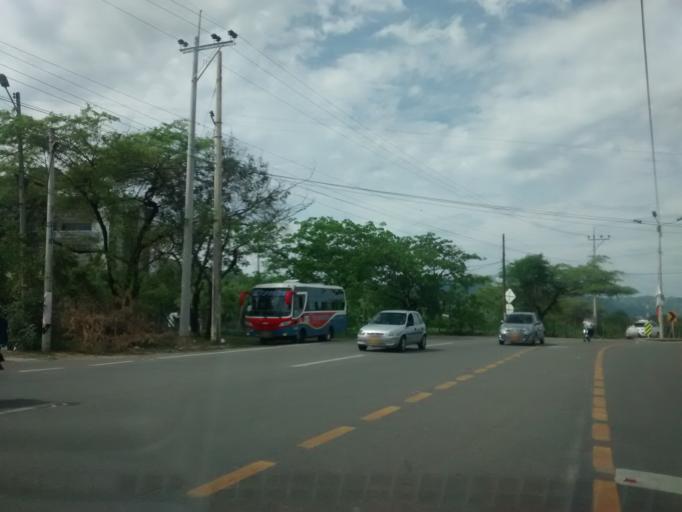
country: CO
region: Cundinamarca
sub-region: Girardot
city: Girardot City
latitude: 4.3162
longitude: -74.8047
